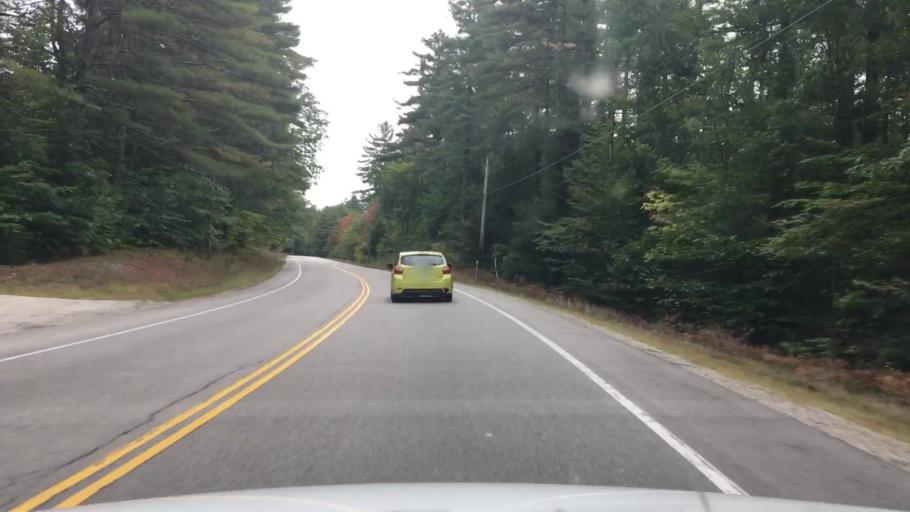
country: US
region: New Hampshire
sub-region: Carroll County
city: Tamworth
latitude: 43.9128
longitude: -71.2375
